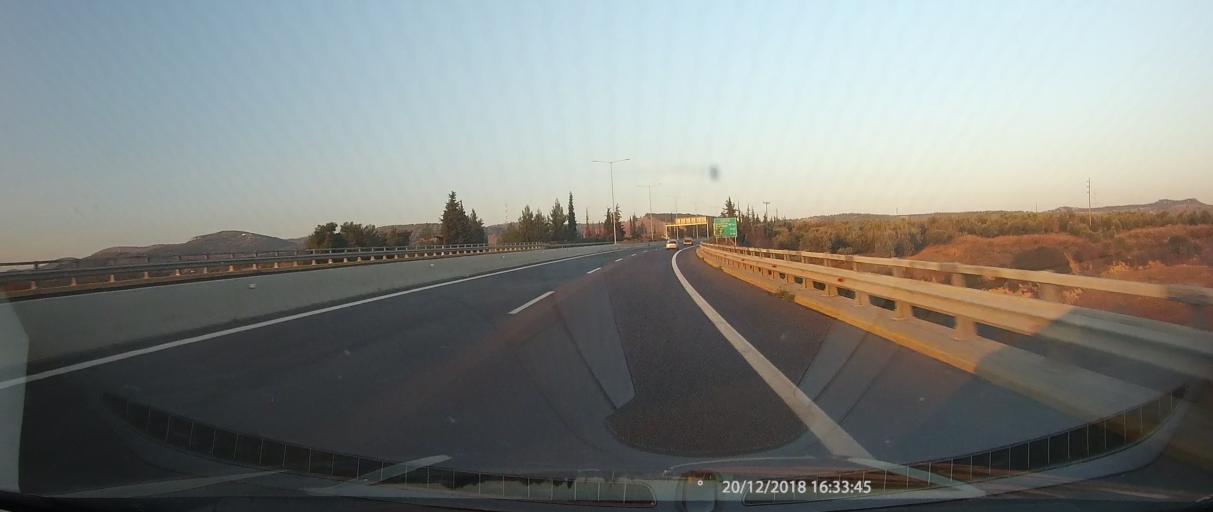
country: GR
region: Thessaly
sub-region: Nomos Magnisias
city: Nea Anchialos
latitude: 39.2703
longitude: 22.7381
